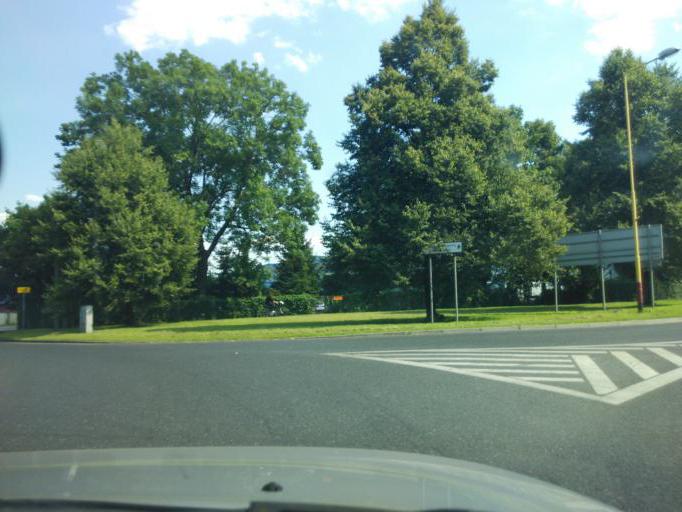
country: PL
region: West Pomeranian Voivodeship
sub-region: Powiat pyrzycki
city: Pyrzyce
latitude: 53.1374
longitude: 14.8938
